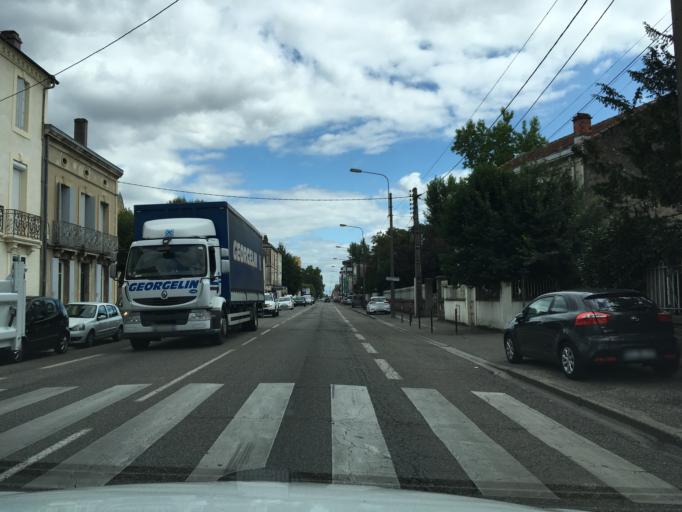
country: FR
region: Aquitaine
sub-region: Departement du Lot-et-Garonne
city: Agen
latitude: 44.2031
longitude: 0.6290
